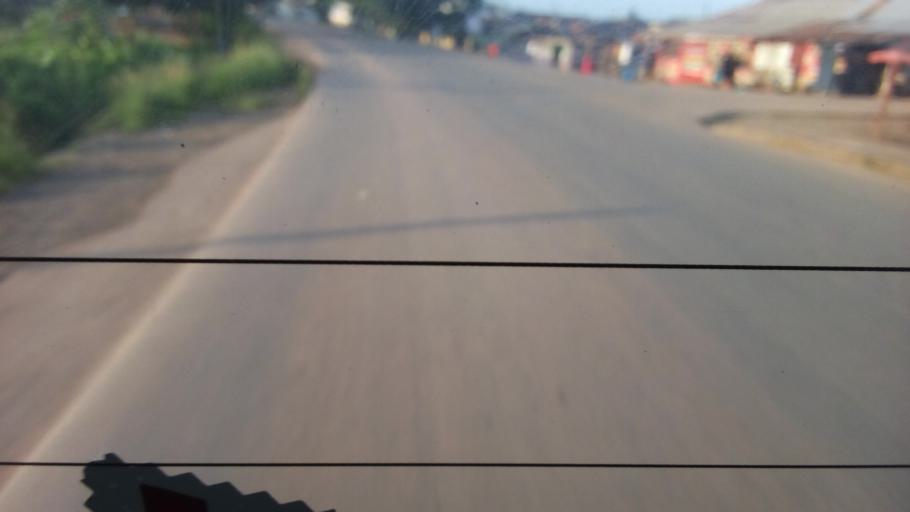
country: GH
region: Western
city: Tarkwa
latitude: 5.1537
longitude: -2.0764
